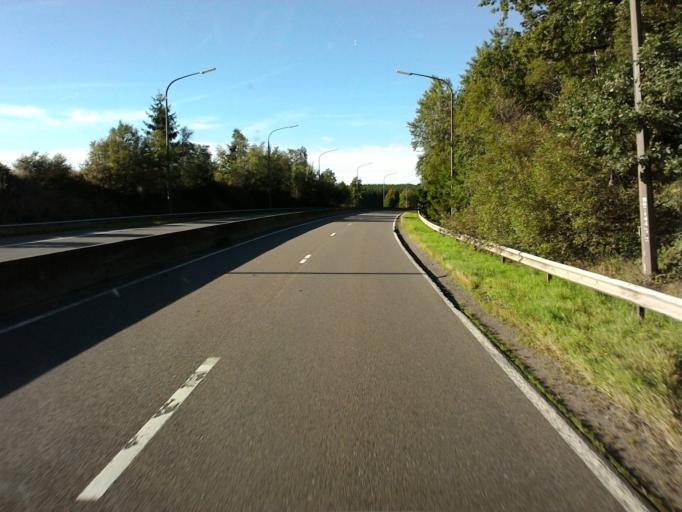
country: BE
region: Wallonia
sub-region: Province du Luxembourg
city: Fauvillers
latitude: 49.8802
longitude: 5.7041
